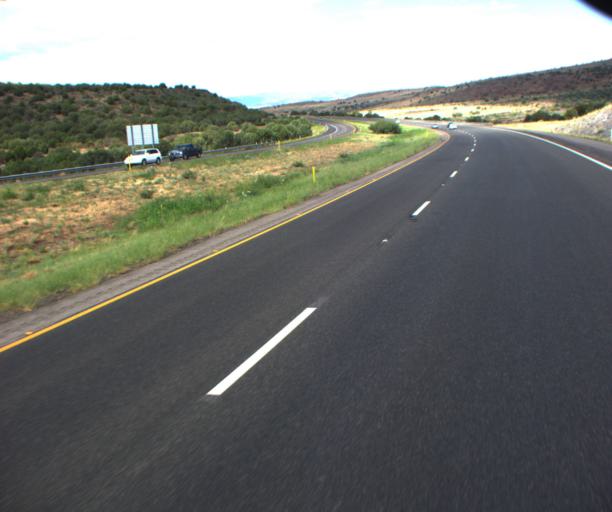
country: US
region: Arizona
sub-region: Yavapai County
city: Camp Verde
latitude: 34.5341
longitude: -111.9715
